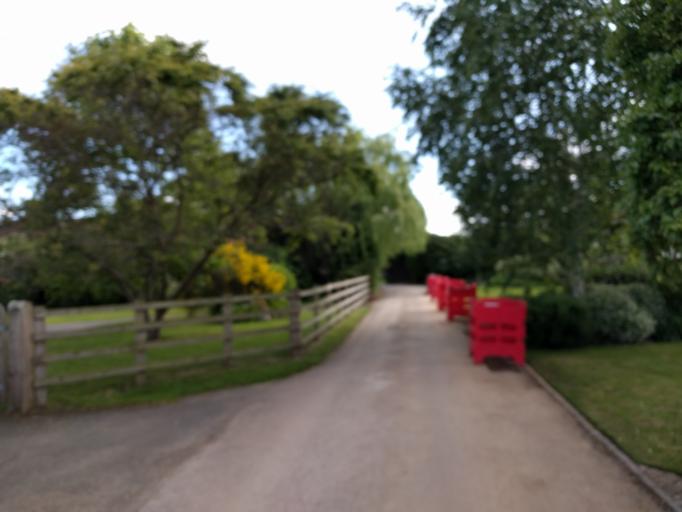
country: GB
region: England
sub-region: Warwickshire
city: Stratford-upon-Avon
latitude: 52.1693
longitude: -1.7147
